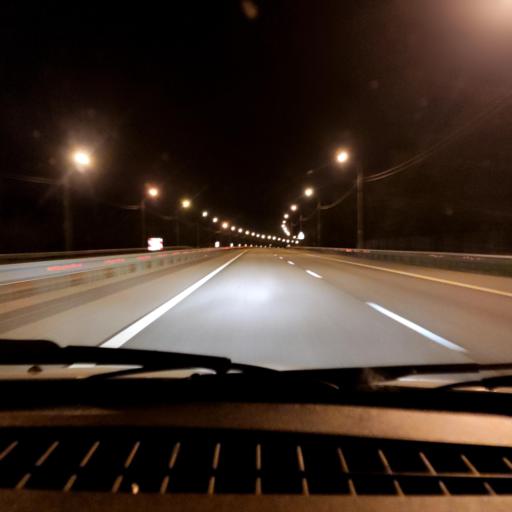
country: RU
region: Lipetsk
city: Zadonsk
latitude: 52.3377
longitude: 38.9739
